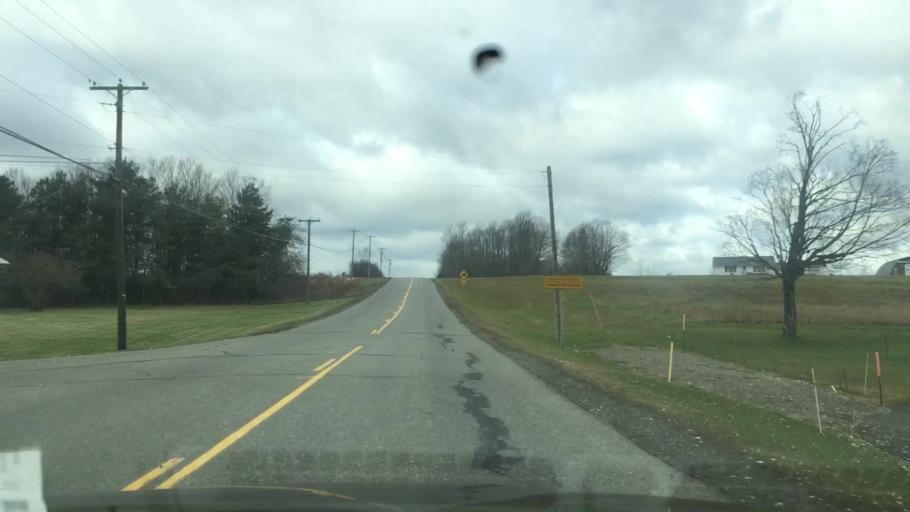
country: US
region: Maine
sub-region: Aroostook County
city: Fort Fairfield
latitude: 46.7597
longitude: -67.7723
